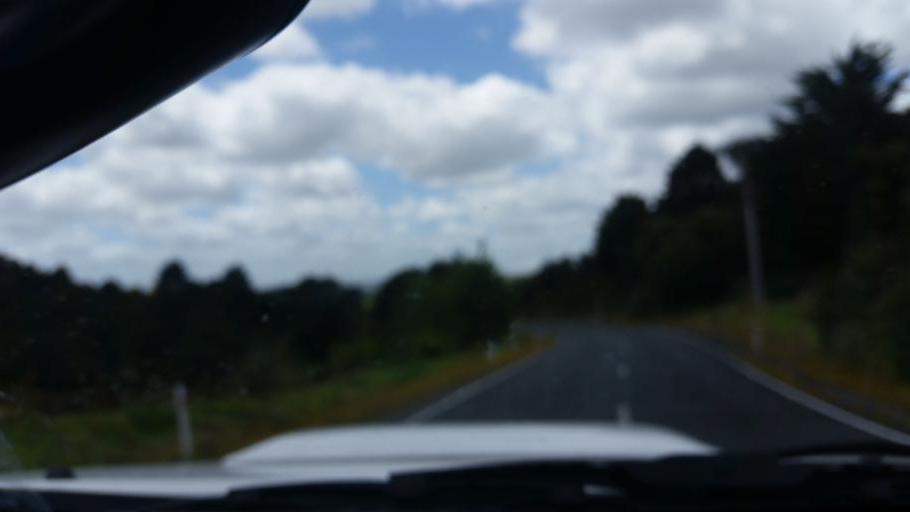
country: NZ
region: Northland
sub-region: Whangarei
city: Ruakaka
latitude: -36.0582
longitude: 174.2725
